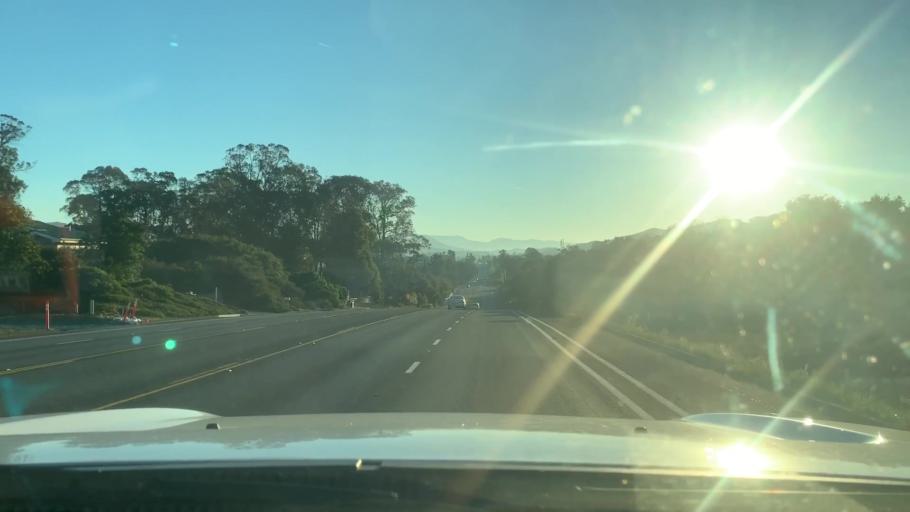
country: US
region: California
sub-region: San Luis Obispo County
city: Los Osos
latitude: 35.3069
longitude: -120.8157
